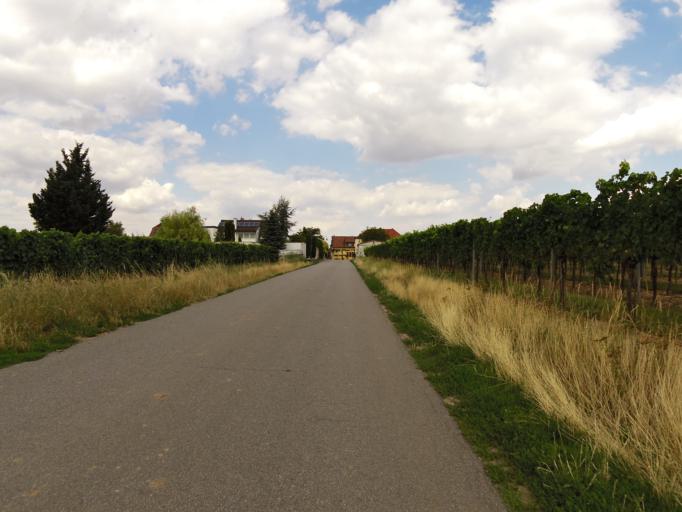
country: DE
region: Rheinland-Pfalz
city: Ellerstadt
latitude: 49.4587
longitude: 8.2596
